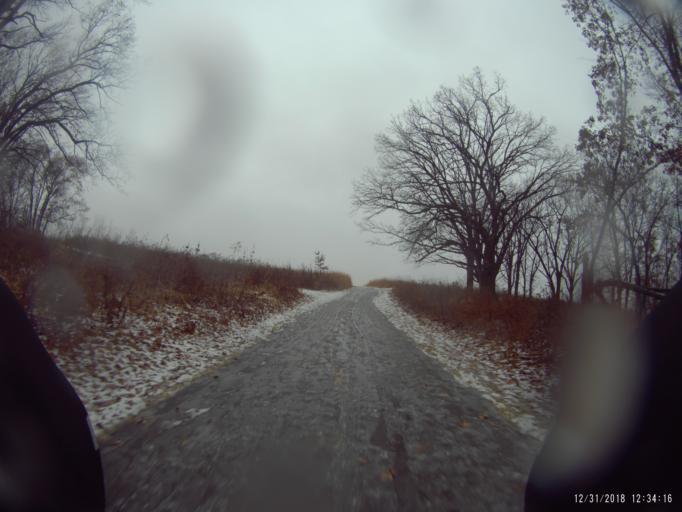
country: US
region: Wisconsin
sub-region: Dane County
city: Verona
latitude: 43.0116
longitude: -89.5175
